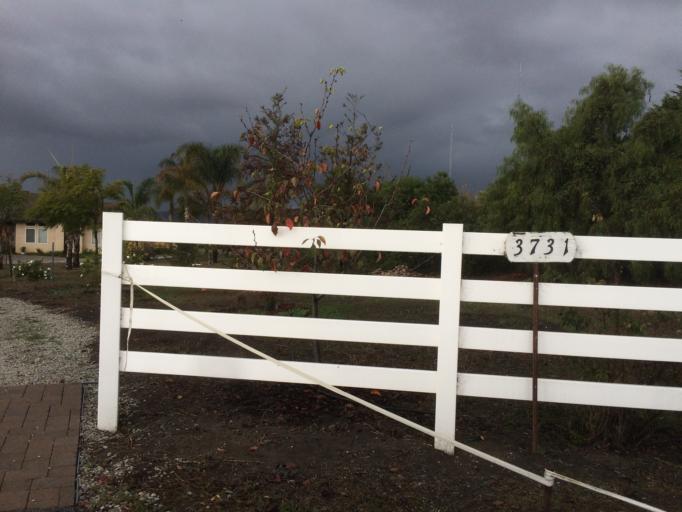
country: US
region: California
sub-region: San Luis Obispo County
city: San Luis Obispo
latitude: 35.2601
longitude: -120.6346
